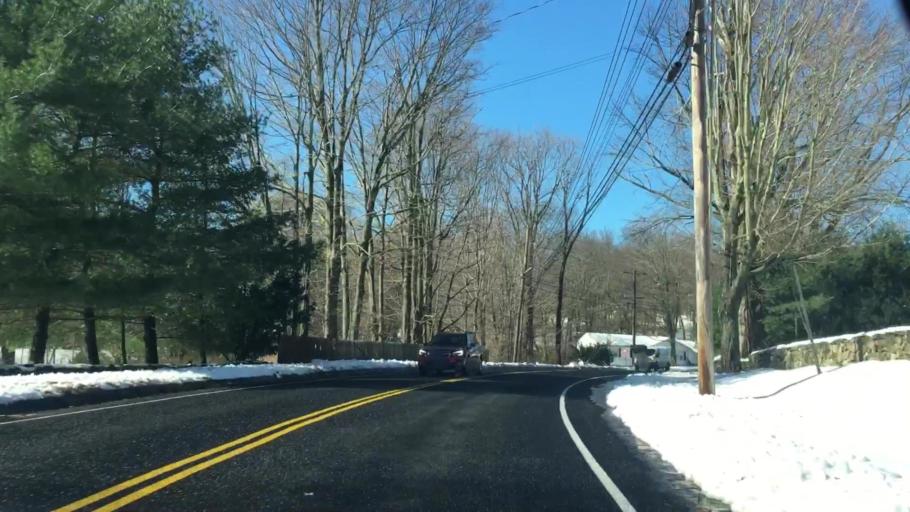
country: US
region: Connecticut
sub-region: Fairfield County
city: Trumbull
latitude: 41.3038
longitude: -73.1640
